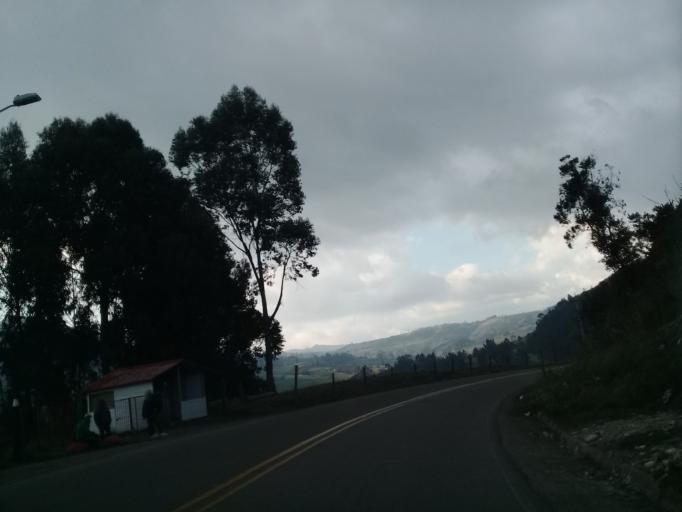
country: CO
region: Cundinamarca
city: Zipaquira
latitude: 5.0567
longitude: -74.0559
